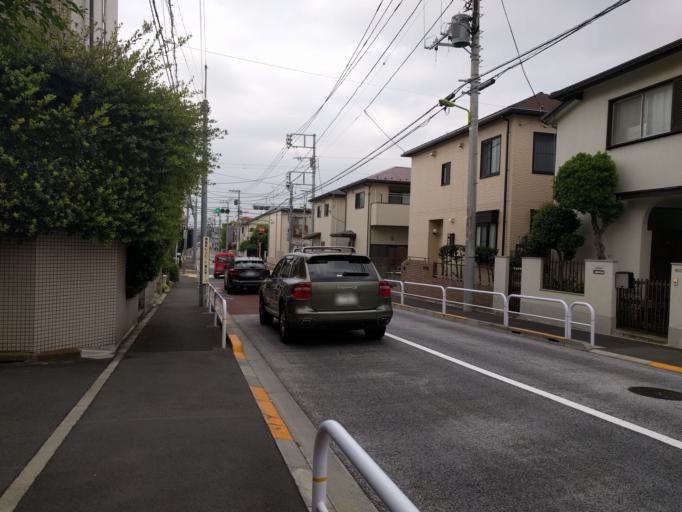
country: JP
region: Tokyo
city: Tokyo
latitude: 35.6037
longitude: 139.6571
